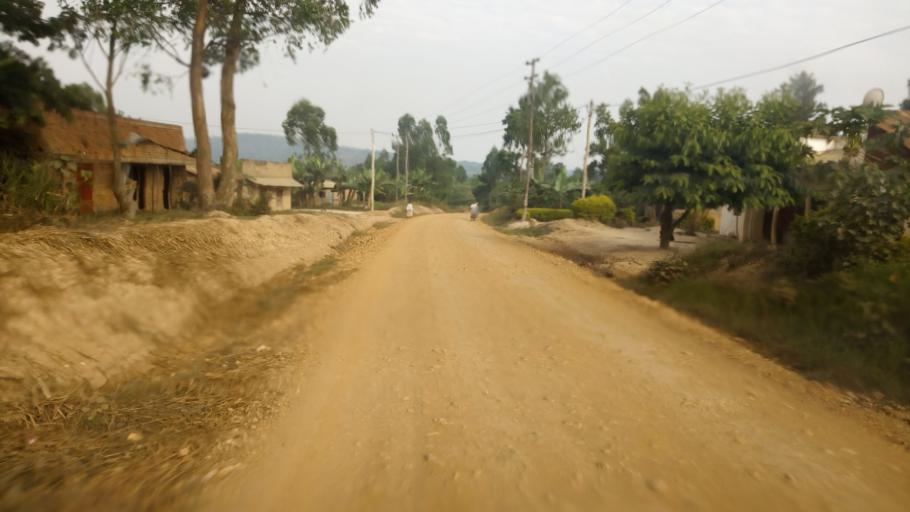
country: UG
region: Western Region
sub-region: Kanungu District
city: Ntungamo
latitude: -0.8391
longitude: 29.6492
